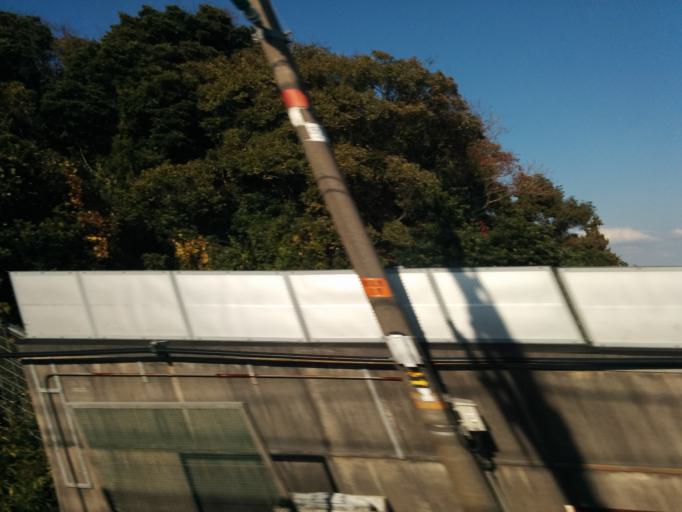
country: JP
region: Shizuoka
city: Kosai-shi
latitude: 34.6990
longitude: 137.5510
